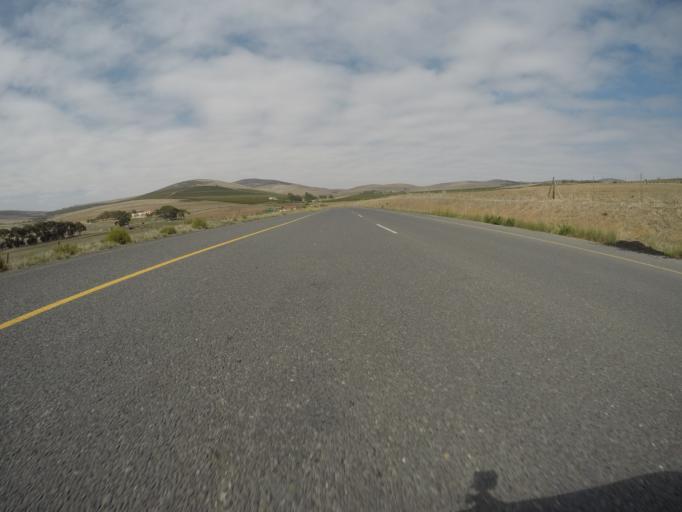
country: ZA
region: Western Cape
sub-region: City of Cape Town
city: Sunset Beach
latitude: -33.7880
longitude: 18.5814
